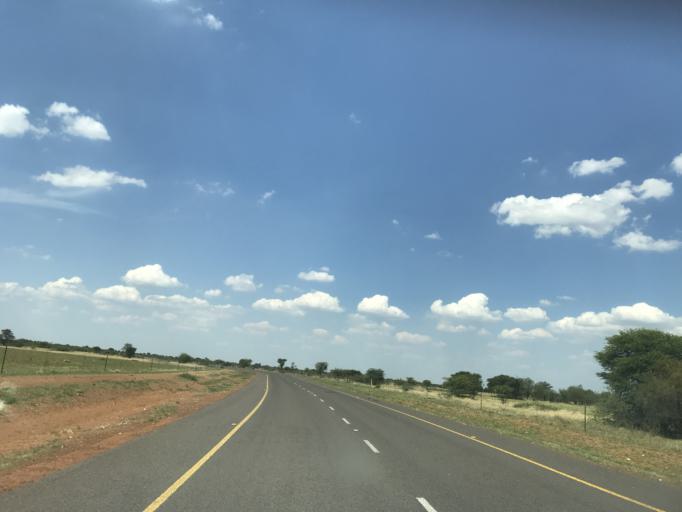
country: BW
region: South East
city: Janeng
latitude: -25.5490
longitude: 25.6048
